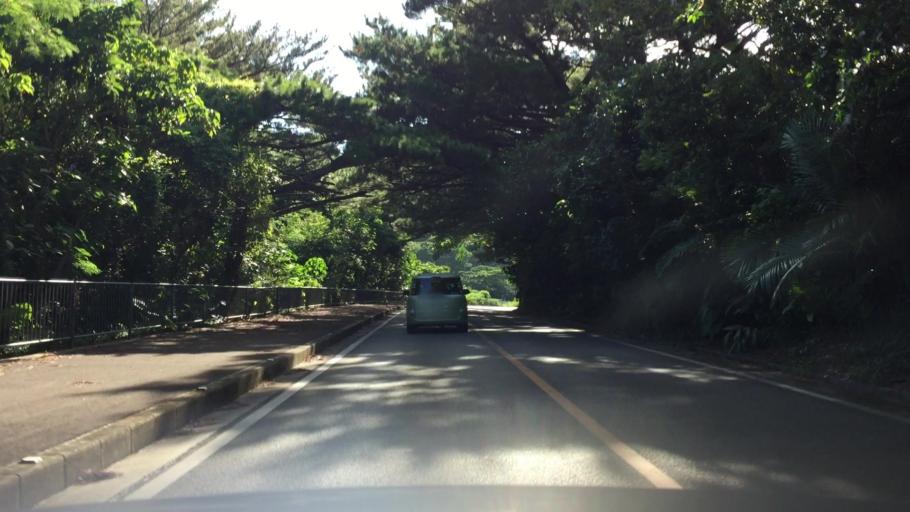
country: JP
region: Okinawa
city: Ishigaki
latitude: 24.4485
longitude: 124.1315
